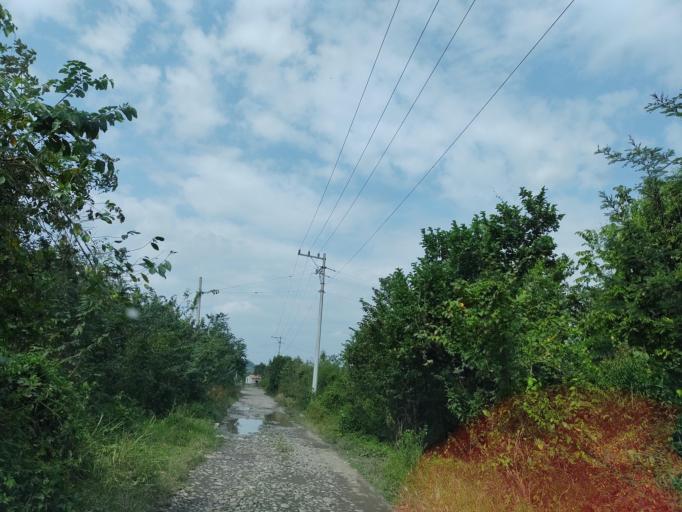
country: MX
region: Puebla
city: Espinal
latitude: 20.2797
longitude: -97.3344
